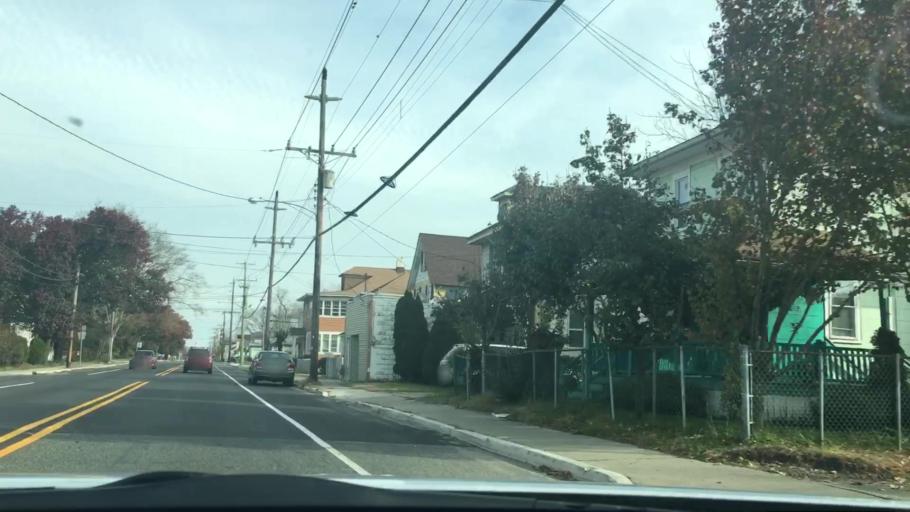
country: US
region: New Jersey
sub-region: Atlantic County
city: Pleasantville
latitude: 39.3948
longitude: -74.5287
